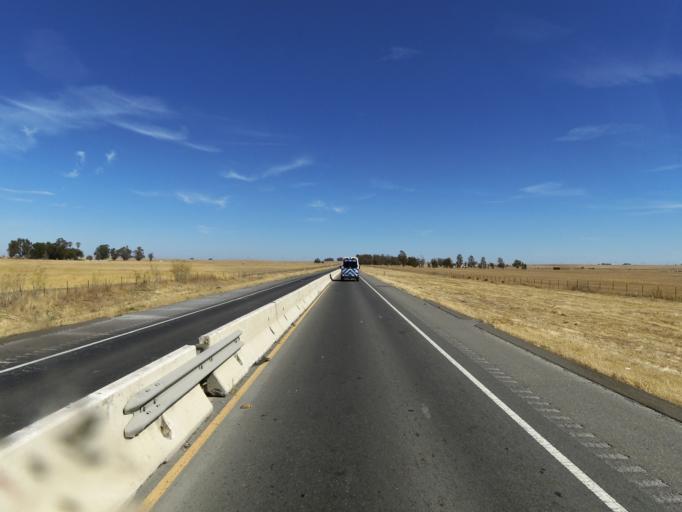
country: US
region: California
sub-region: Solano County
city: Suisun
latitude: 38.2284
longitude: -121.9142
